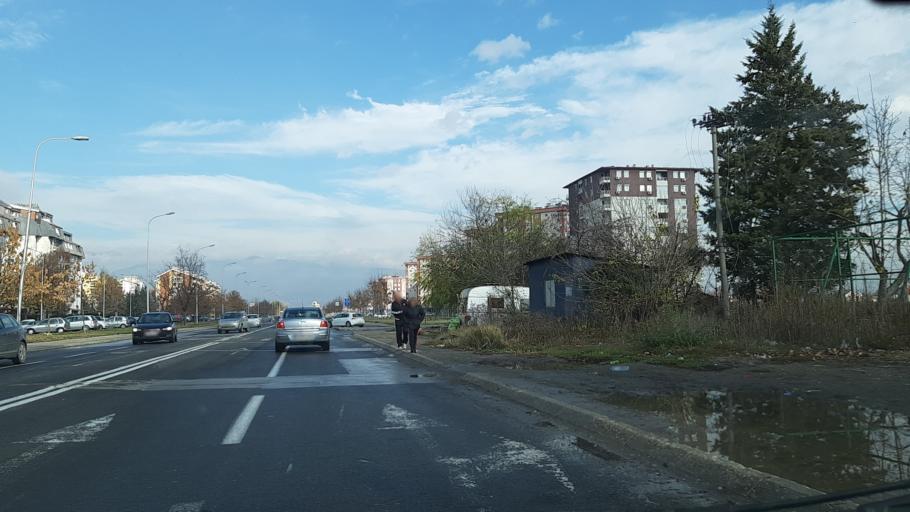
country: MK
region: Kisela Voda
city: Usje
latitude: 41.9798
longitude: 21.4791
